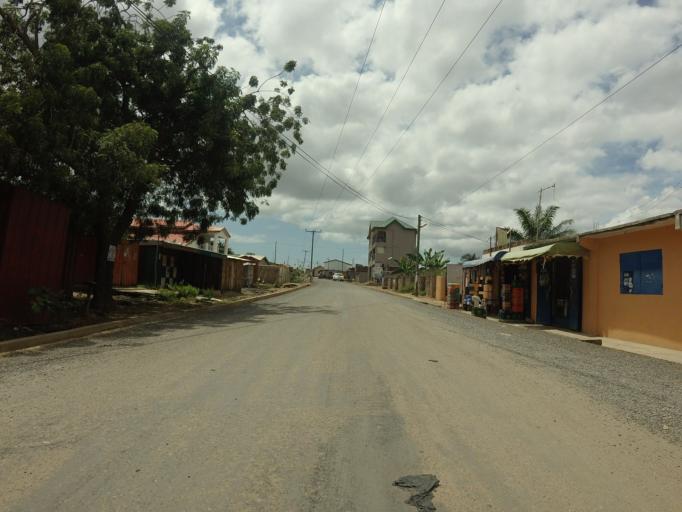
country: GH
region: Central
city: Kasoa
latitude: 5.5445
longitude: -0.3985
